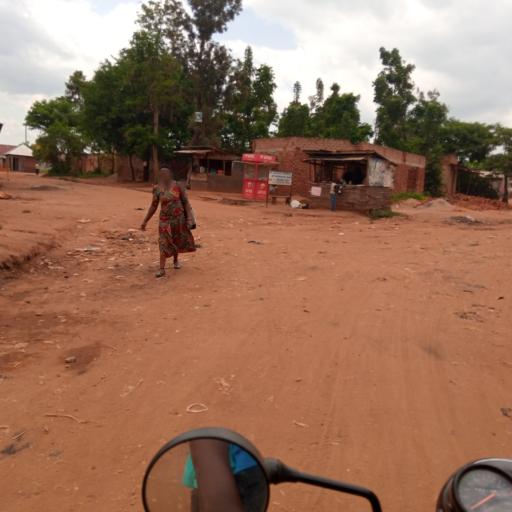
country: UG
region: Eastern Region
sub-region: Mbale District
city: Mbale
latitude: 1.1015
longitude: 34.1802
